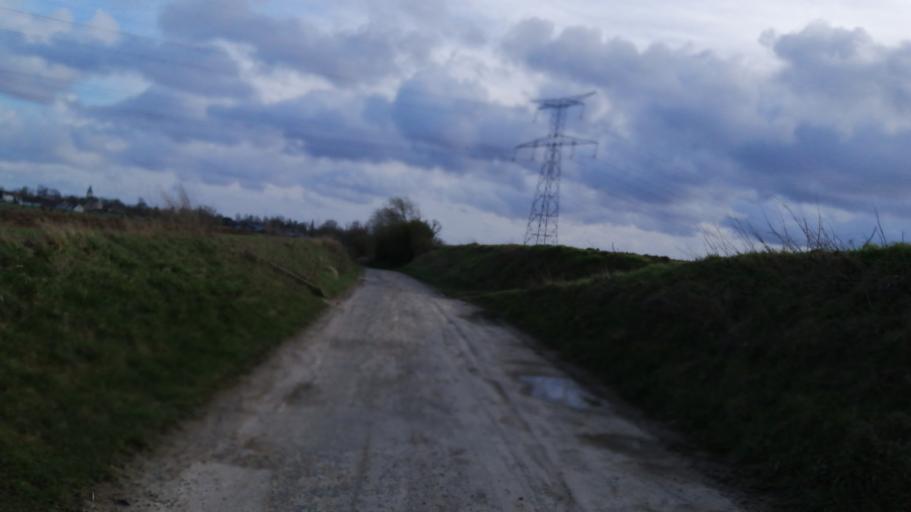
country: FR
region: Nord-Pas-de-Calais
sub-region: Departement du Pas-de-Calais
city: Beaurains
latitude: 50.2438
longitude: 2.7873
